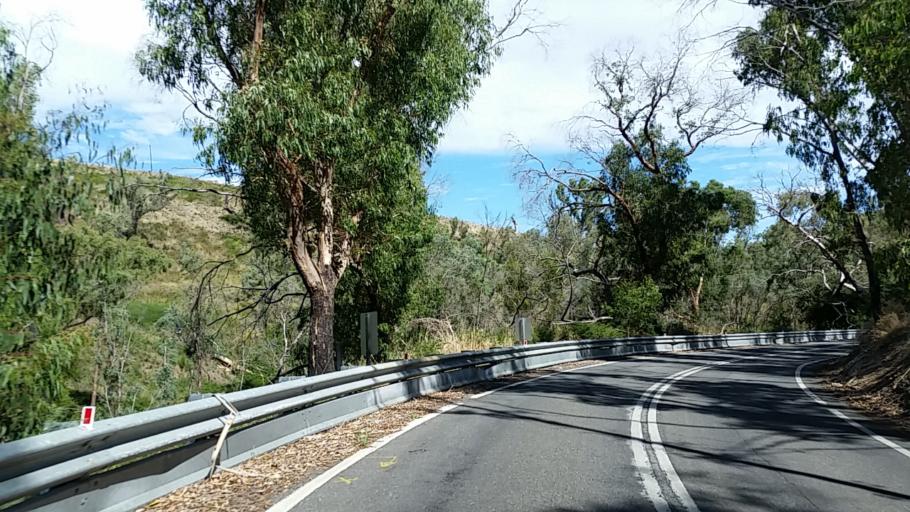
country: AU
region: South Australia
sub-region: Adelaide Hills
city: Gumeracha
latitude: -34.8267
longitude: 138.8521
